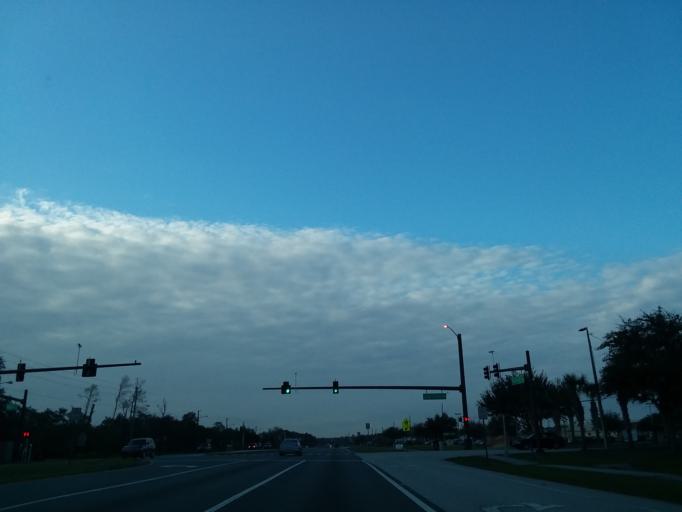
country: US
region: Florida
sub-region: Osceola County
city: Poinciana
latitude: 28.1641
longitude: -81.4402
